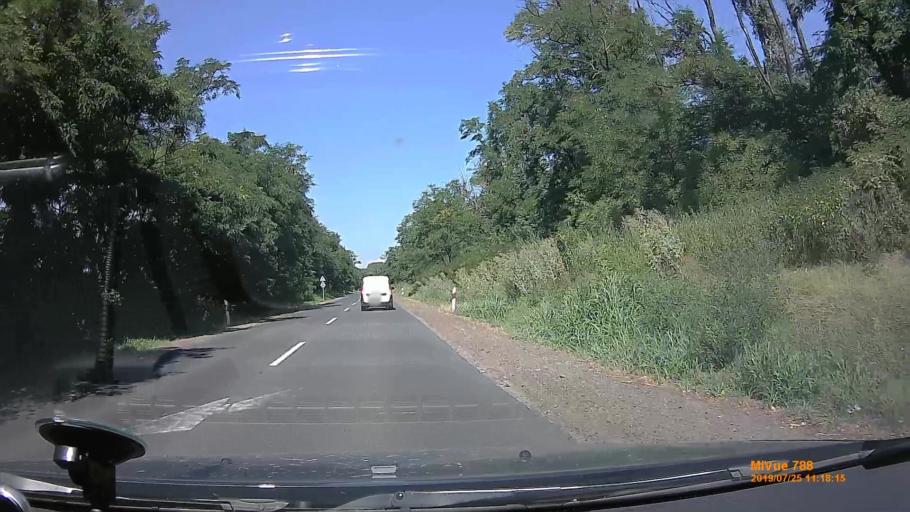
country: HU
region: Szabolcs-Szatmar-Bereg
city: Nagykallo
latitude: 47.8965
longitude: 21.7984
